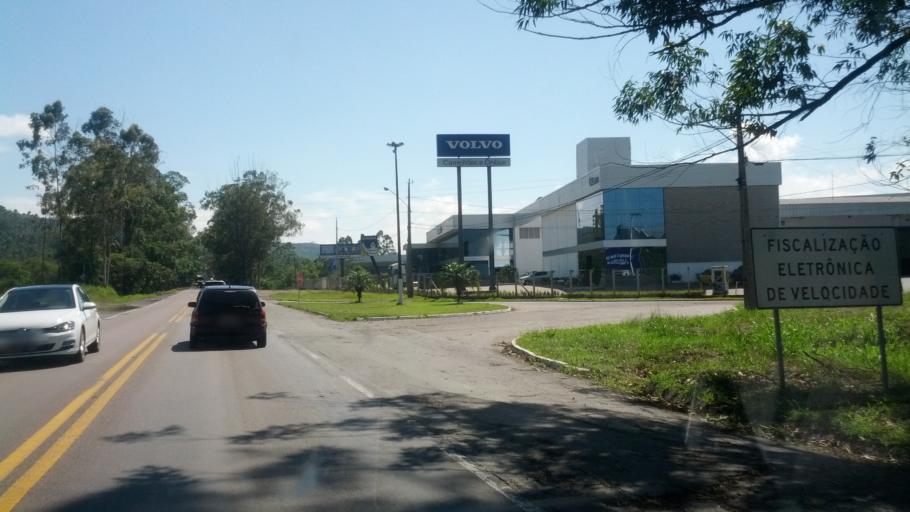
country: BR
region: Santa Catarina
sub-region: Rio Do Sul
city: Rio do Sul
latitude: -27.1786
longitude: -49.5953
